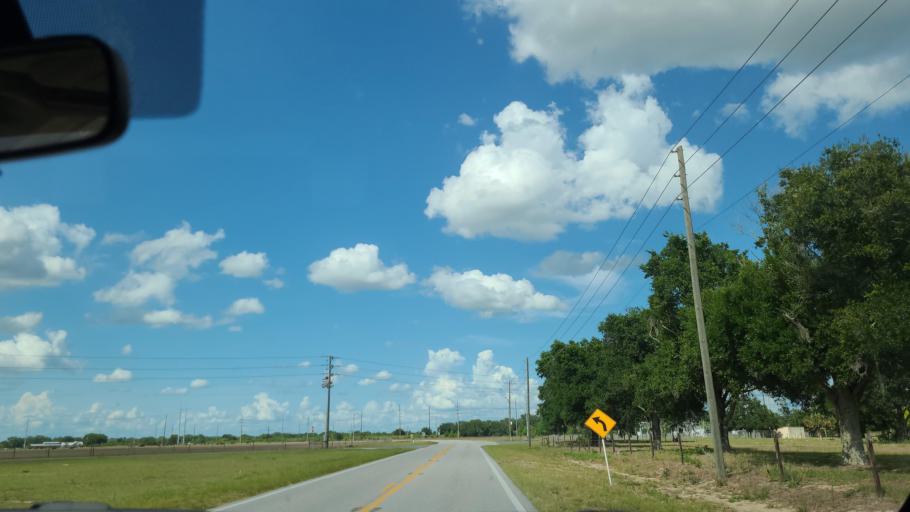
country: US
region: Florida
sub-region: Polk County
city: Lake Wales
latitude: 27.9241
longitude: -81.5405
